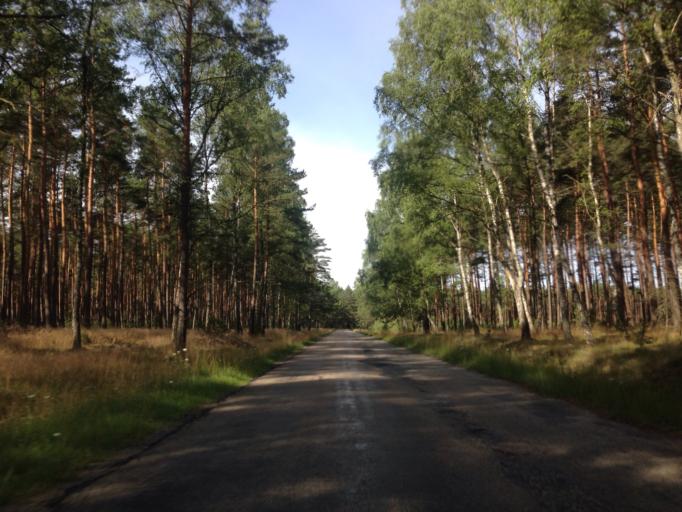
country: PL
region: Kujawsko-Pomorskie
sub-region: Powiat swiecki
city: Osie
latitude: 53.6986
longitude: 18.3268
